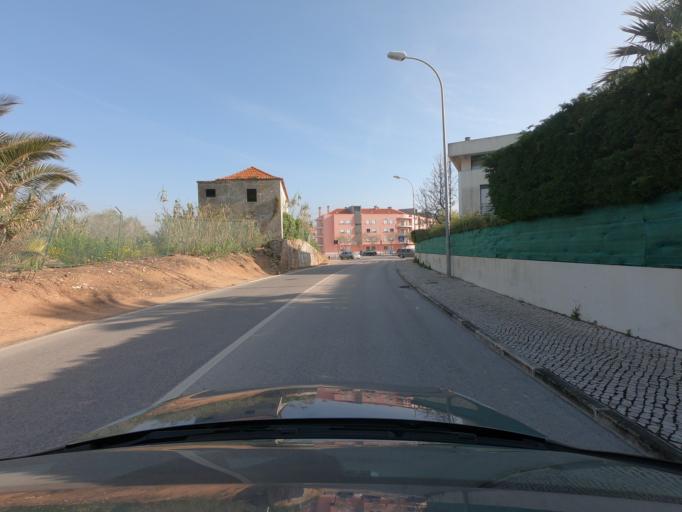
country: PT
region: Lisbon
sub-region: Oeiras
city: Carcavelos
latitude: 38.6828
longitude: -9.3245
